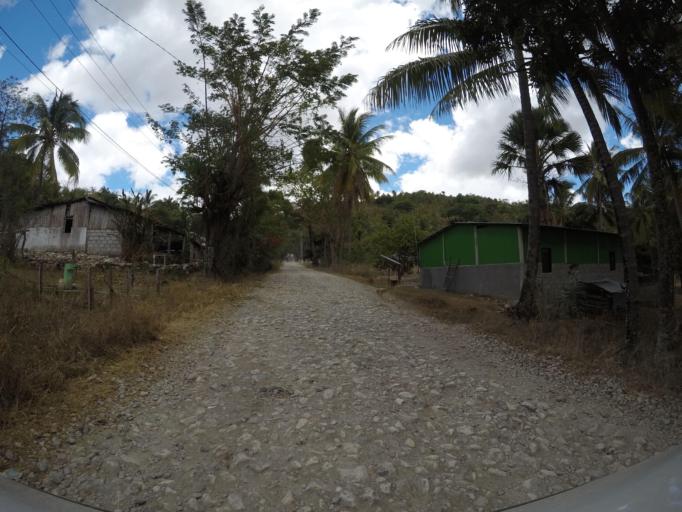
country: TL
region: Baucau
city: Baucau
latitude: -8.5081
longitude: 126.6787
